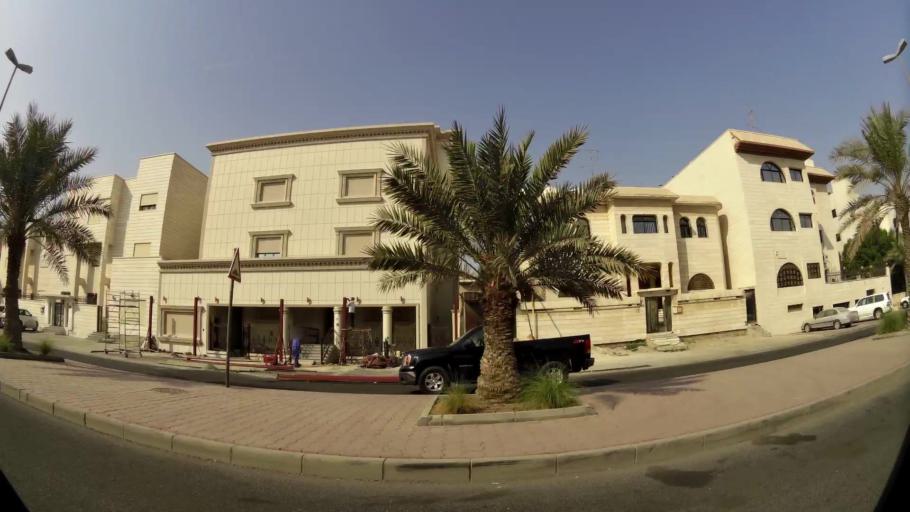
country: KW
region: Al Asimah
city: Ar Rabiyah
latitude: 29.2699
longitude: 47.8698
